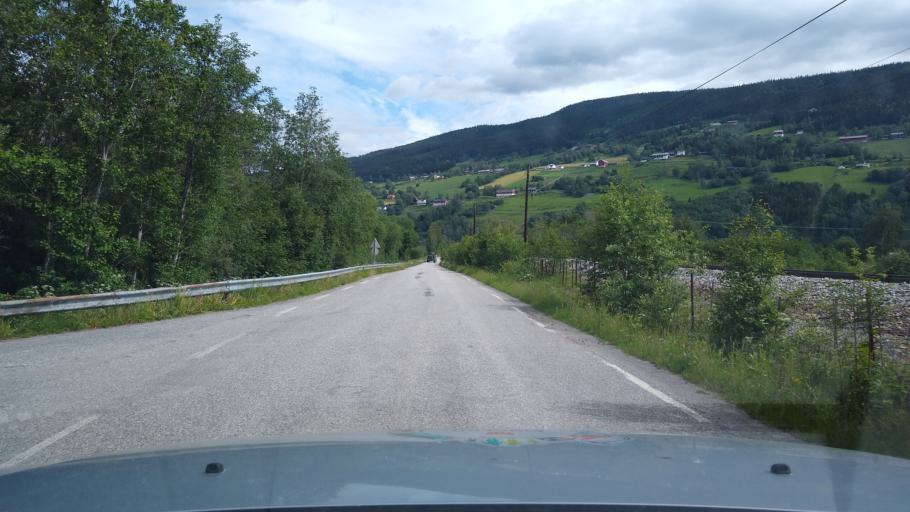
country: NO
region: Oppland
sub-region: Ringebu
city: Ringebu
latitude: 61.5202
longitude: 10.1434
